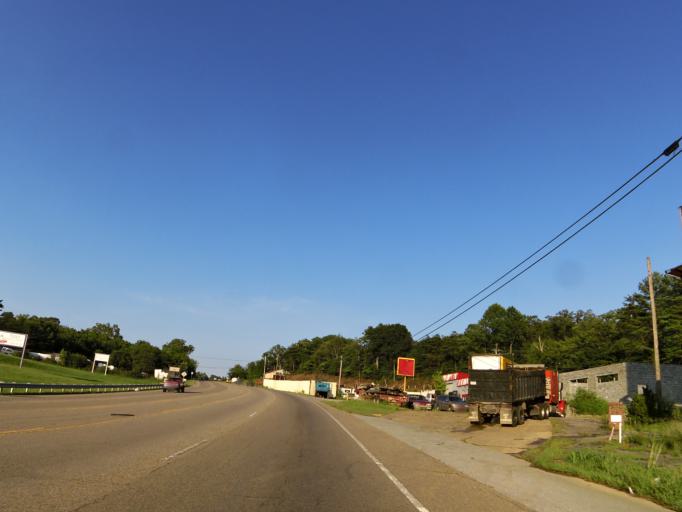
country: US
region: Tennessee
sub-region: Anderson County
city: Clinton
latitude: 36.0277
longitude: -84.0735
